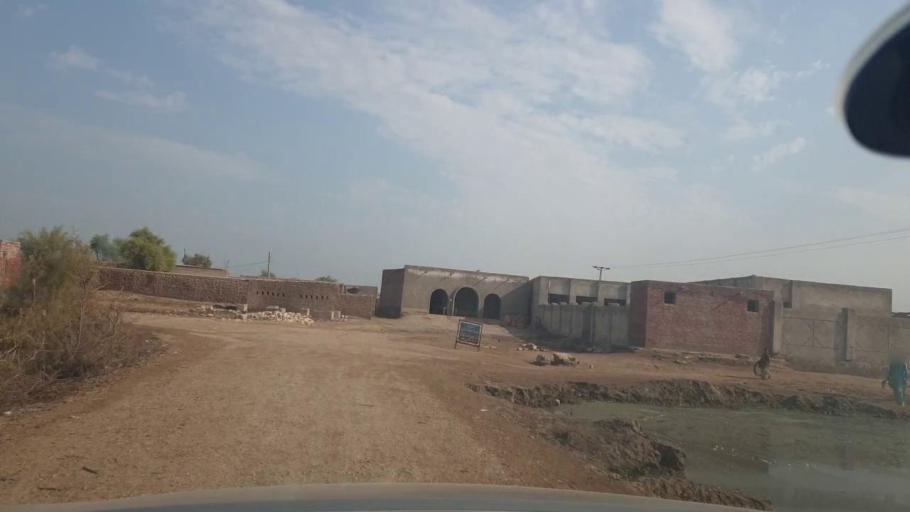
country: PK
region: Balochistan
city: Mehrabpur
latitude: 28.0734
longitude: 68.2110
